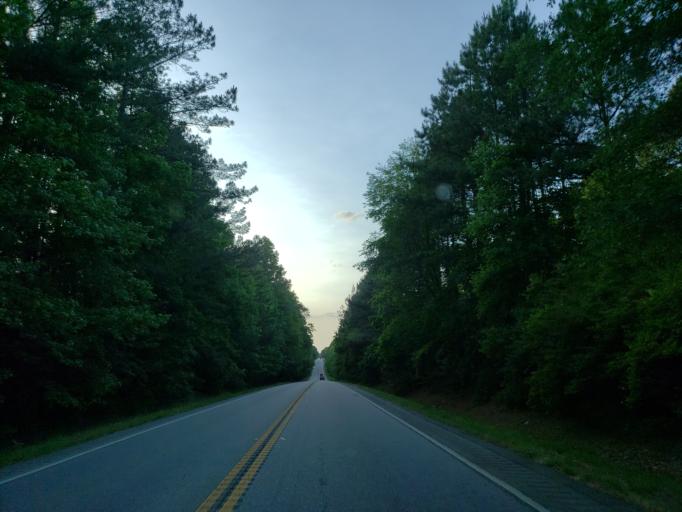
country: US
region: Georgia
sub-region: Coweta County
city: Newnan
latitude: 33.4495
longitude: -84.8825
